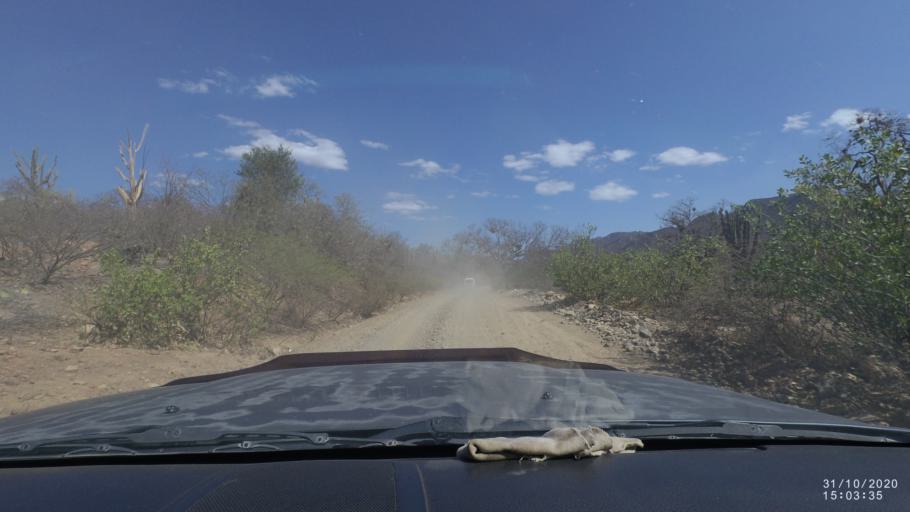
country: BO
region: Cochabamba
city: Aiquile
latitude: -18.2763
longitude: -64.8056
